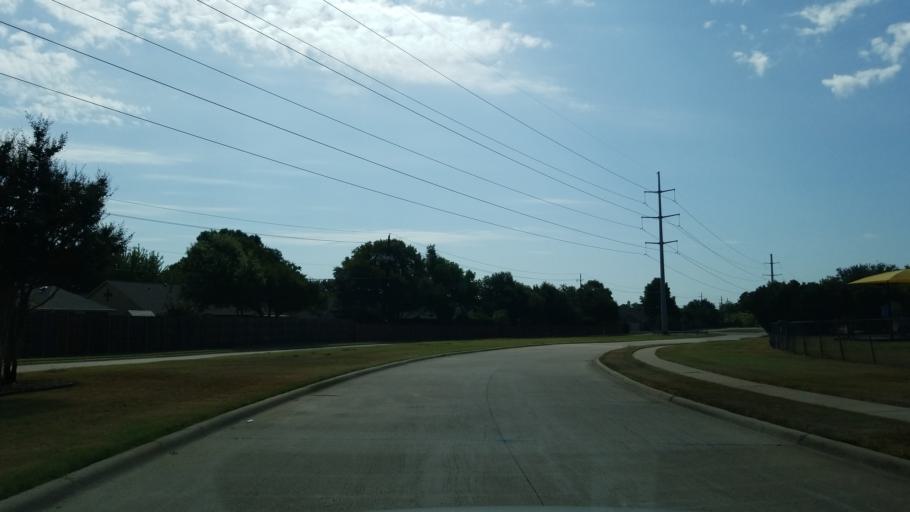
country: US
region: Texas
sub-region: Tarrant County
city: Euless
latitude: 32.8840
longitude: -97.0957
